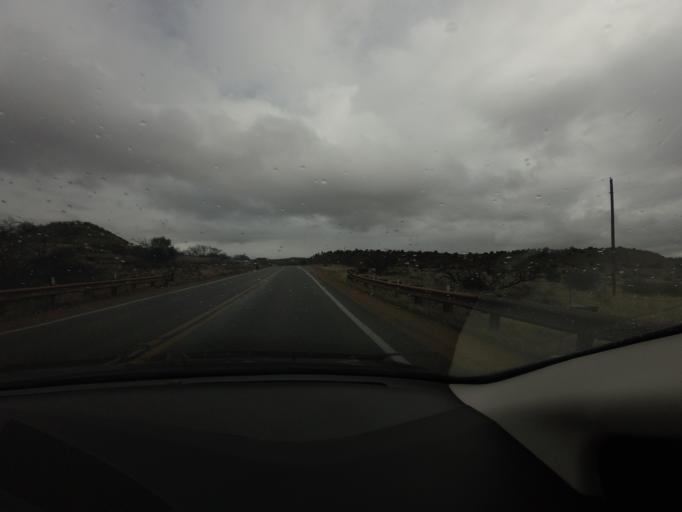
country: US
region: Arizona
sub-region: Yavapai County
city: Cornville
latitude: 34.7062
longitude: -111.8752
